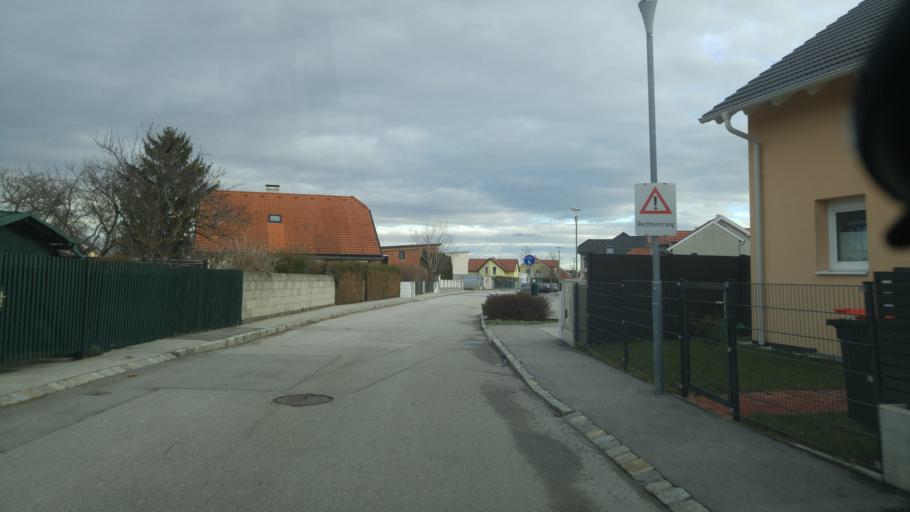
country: AT
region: Lower Austria
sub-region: Politischer Bezirk Baden
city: Bad Voslau
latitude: 47.9590
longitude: 16.2087
